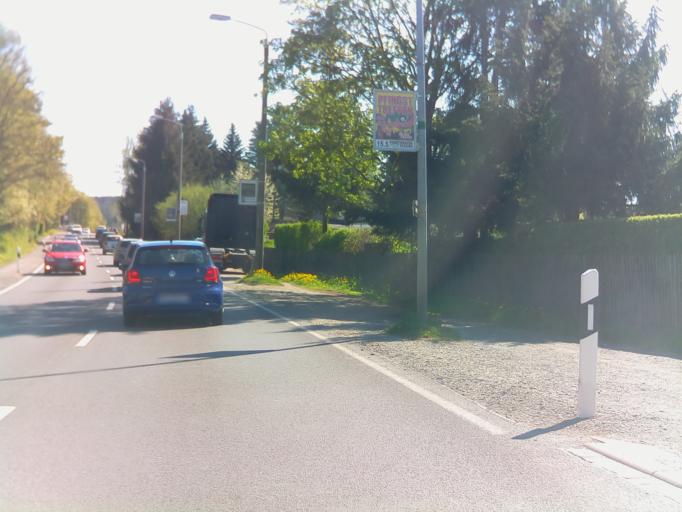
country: DE
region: Saxony
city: Plauen
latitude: 50.4960
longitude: 12.1750
